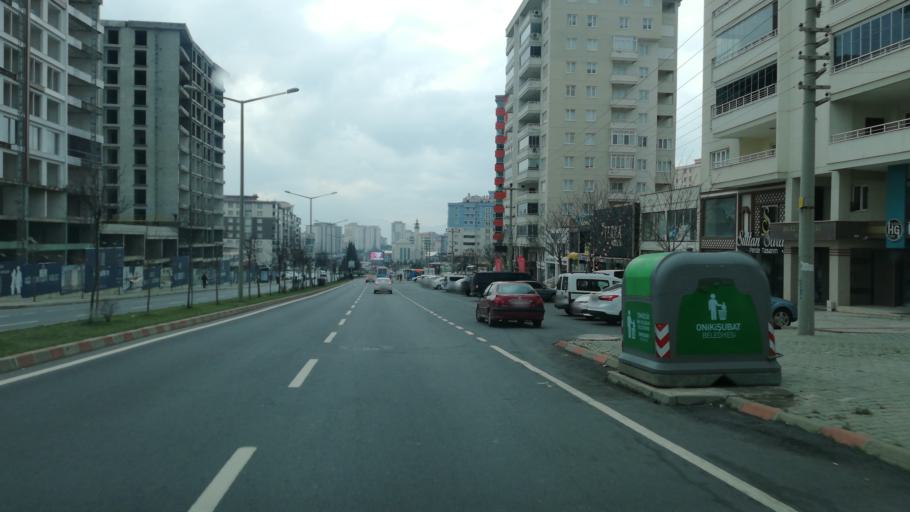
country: TR
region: Kahramanmaras
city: Kahramanmaras
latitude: 37.5831
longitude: 36.8733
